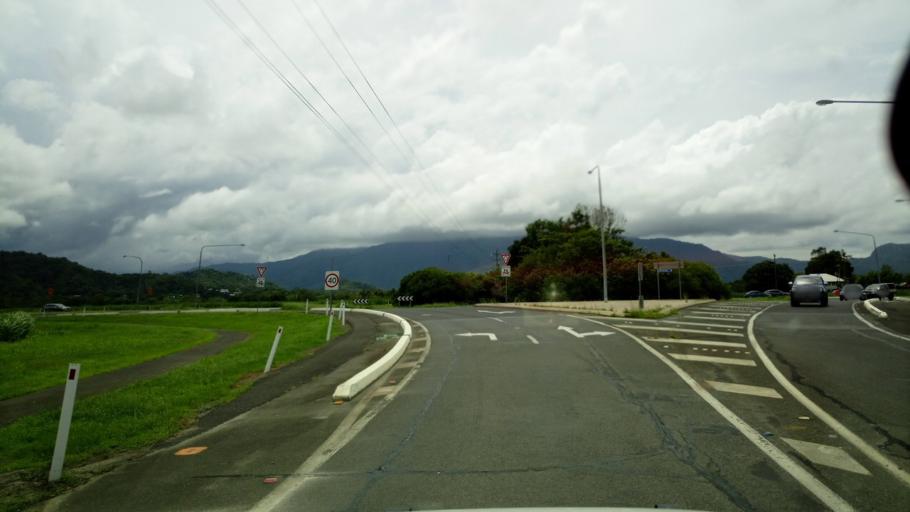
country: AU
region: Queensland
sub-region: Cairns
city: Redlynch
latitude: -16.8633
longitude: 145.7323
